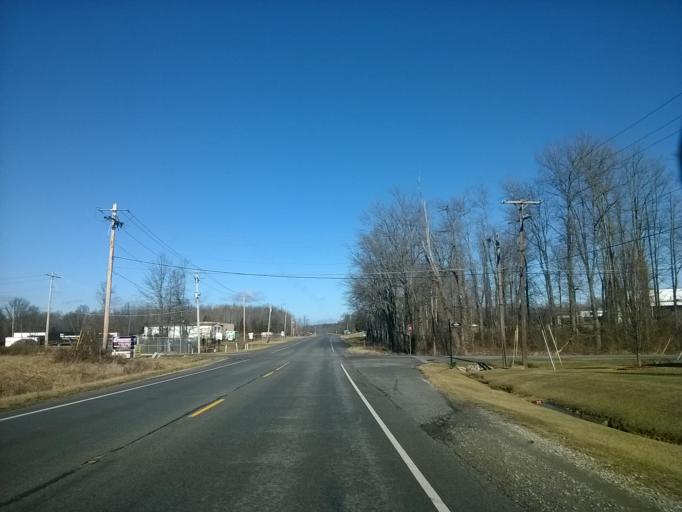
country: US
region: Indiana
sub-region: Scott County
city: Austin
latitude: 38.7572
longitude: -85.8136
